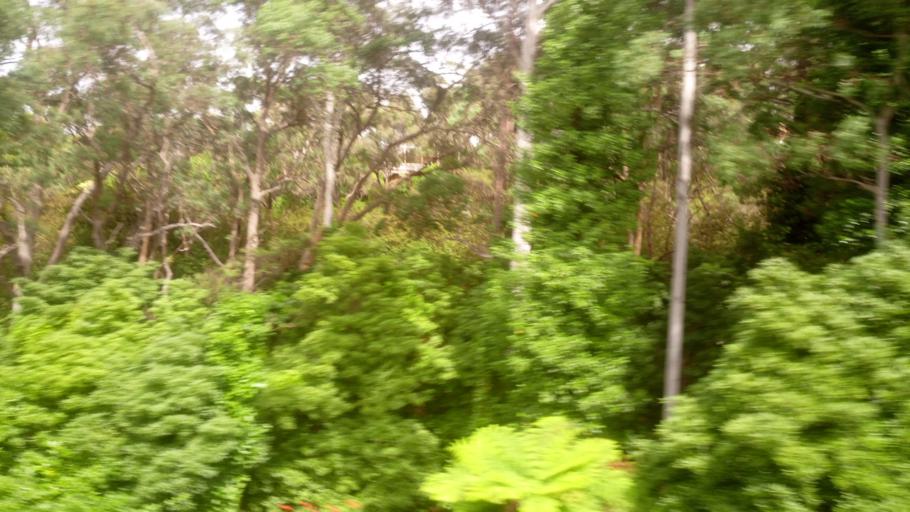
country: AU
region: New South Wales
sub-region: Blue Mountains Municipality
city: Lawson
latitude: -33.7210
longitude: 150.3862
